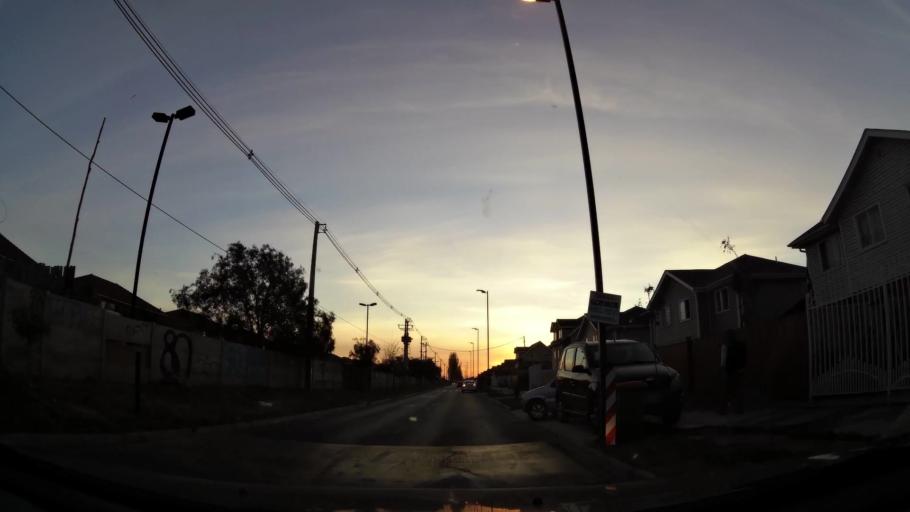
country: CL
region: Santiago Metropolitan
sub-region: Provincia de Cordillera
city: Puente Alto
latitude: -33.5998
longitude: -70.5907
